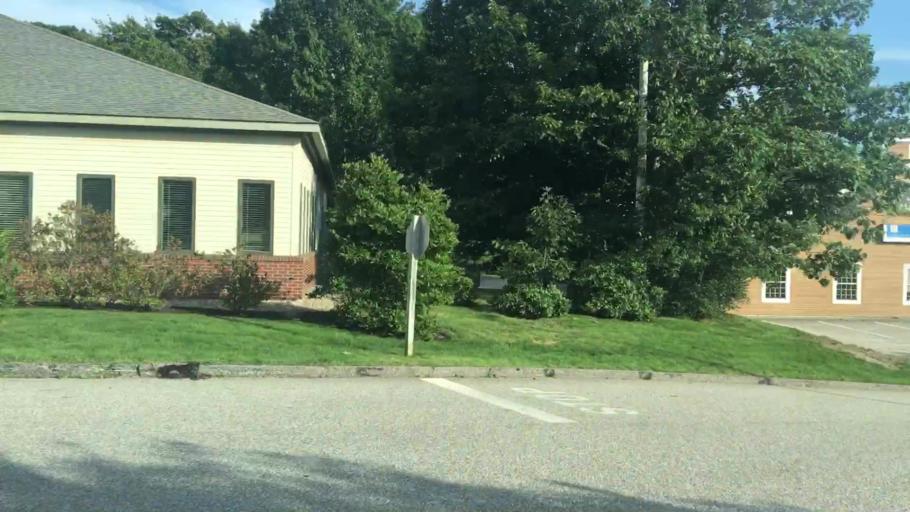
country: US
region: Maine
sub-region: Cumberland County
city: Scarborough
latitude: 43.5978
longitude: -70.3230
